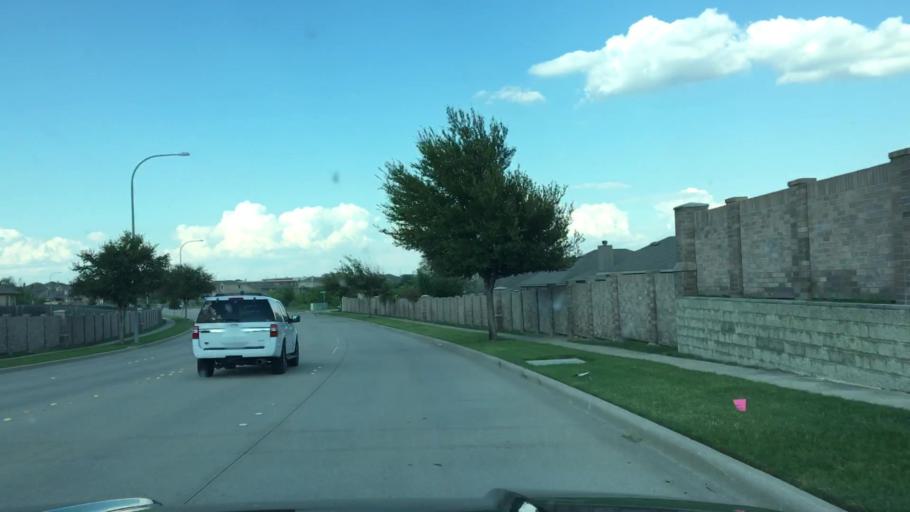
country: US
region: Texas
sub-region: Tarrant County
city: Haslet
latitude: 32.9867
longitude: -97.3712
